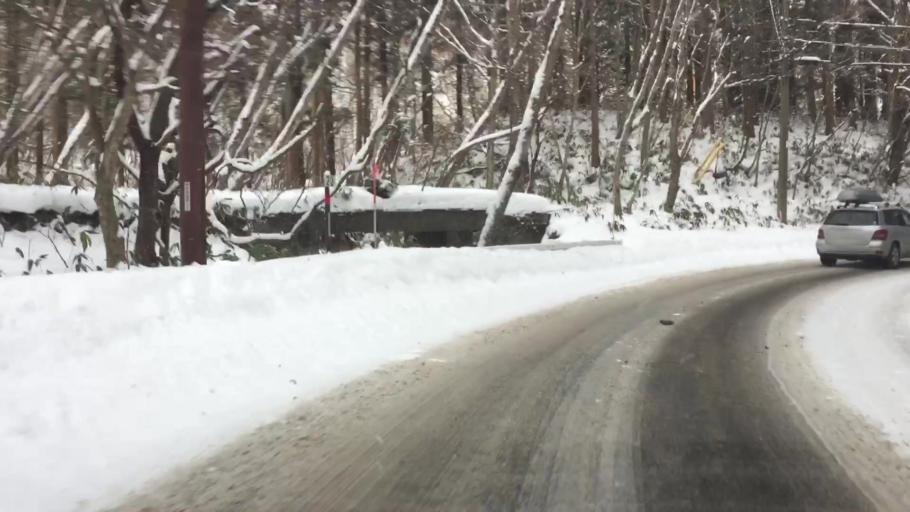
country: JP
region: Tochigi
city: Yaita
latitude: 36.9535
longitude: 139.7767
